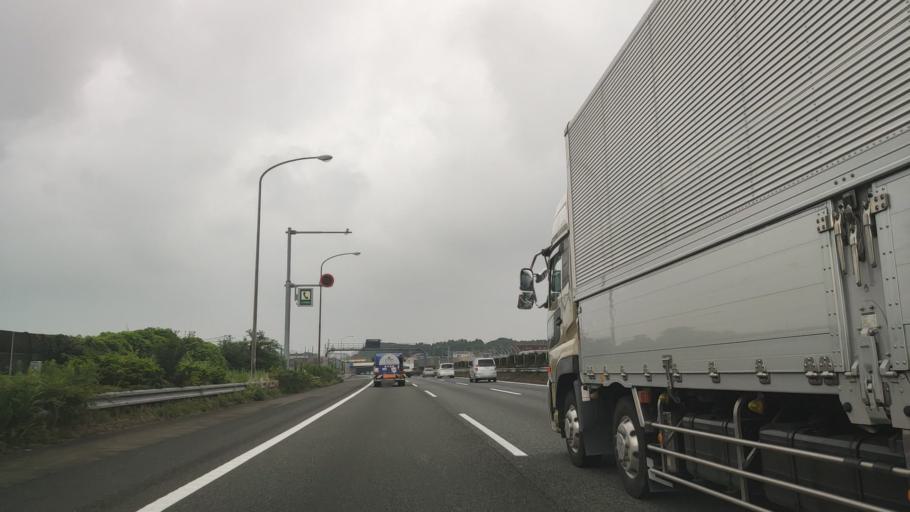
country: JP
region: Kanagawa
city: Minami-rinkan
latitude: 35.4789
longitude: 139.4543
